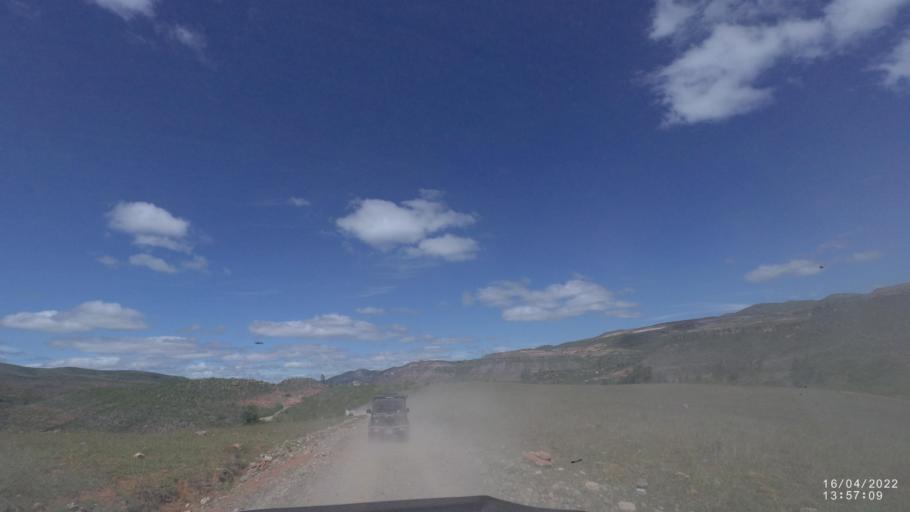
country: BO
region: Cochabamba
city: Mizque
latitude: -18.0361
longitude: -65.5620
